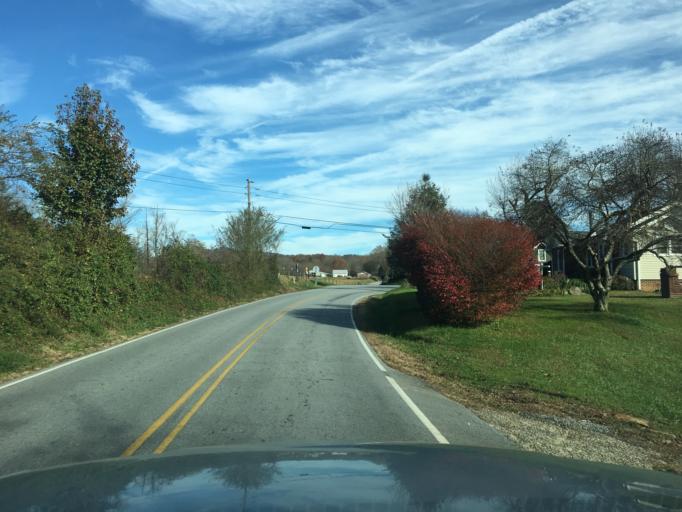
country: US
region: North Carolina
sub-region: Henderson County
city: Etowah
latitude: 35.3230
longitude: -82.5957
